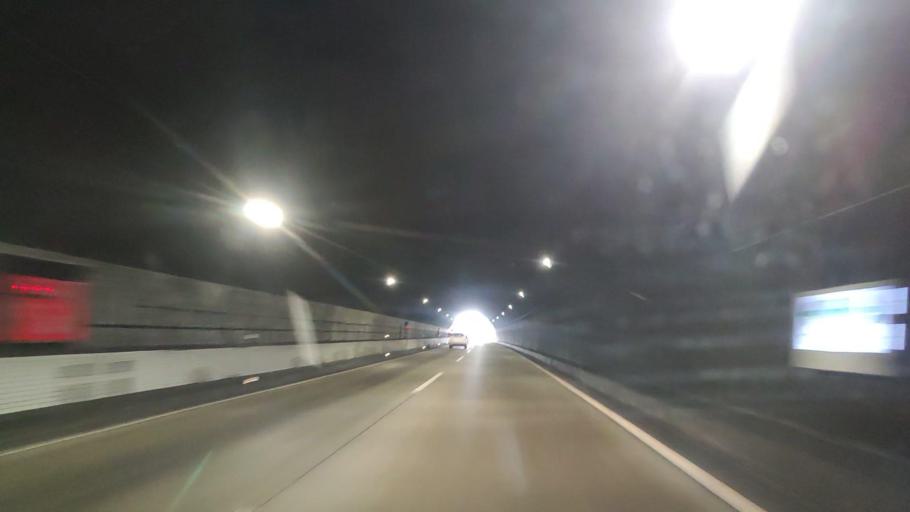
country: JP
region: Okayama
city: Kamogatacho-kamogata
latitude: 34.5580
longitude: 133.6158
